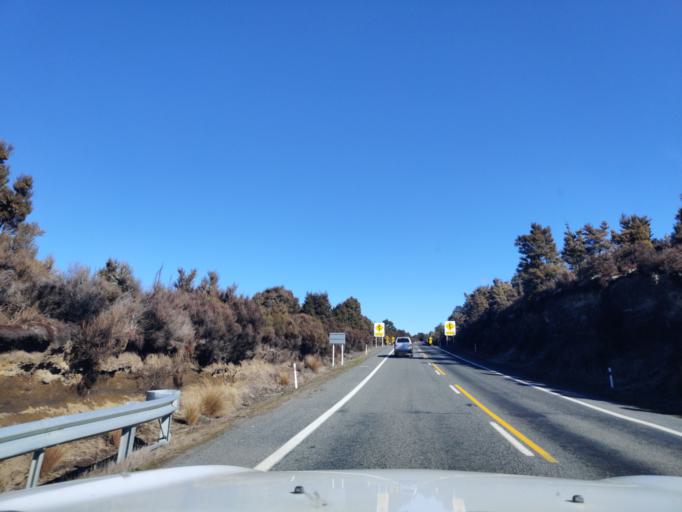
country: NZ
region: Waikato
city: Turangi
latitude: -39.2119
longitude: 175.7443
